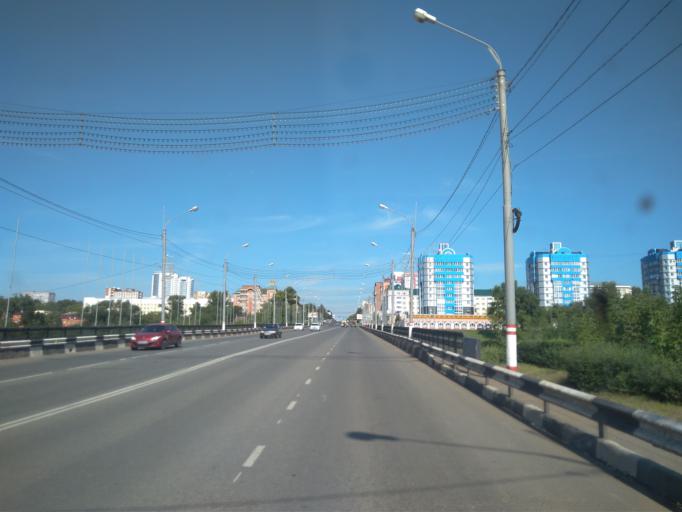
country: RU
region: Mordoviya
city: Saransk
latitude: 54.1791
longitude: 45.1709
